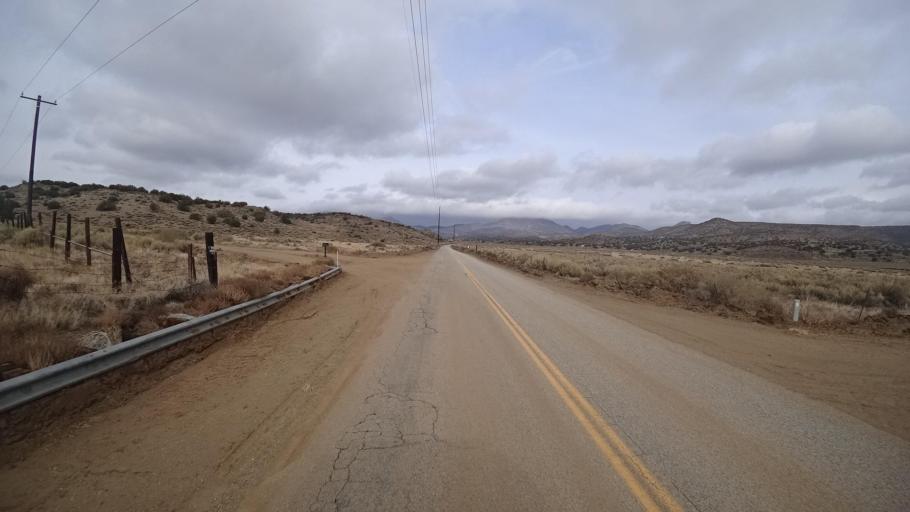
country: US
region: California
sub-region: Kern County
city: Tehachapi
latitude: 35.1540
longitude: -118.3201
